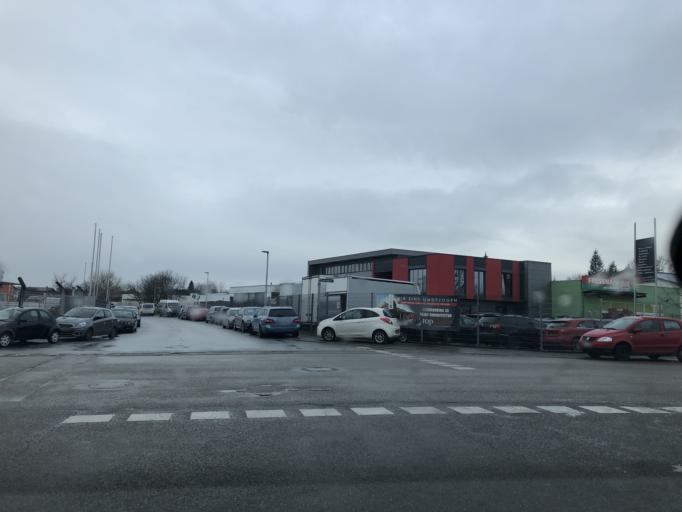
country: DE
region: Baden-Wuerttemberg
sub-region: Karlsruhe Region
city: Rastatt
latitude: 48.8593
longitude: 8.2328
